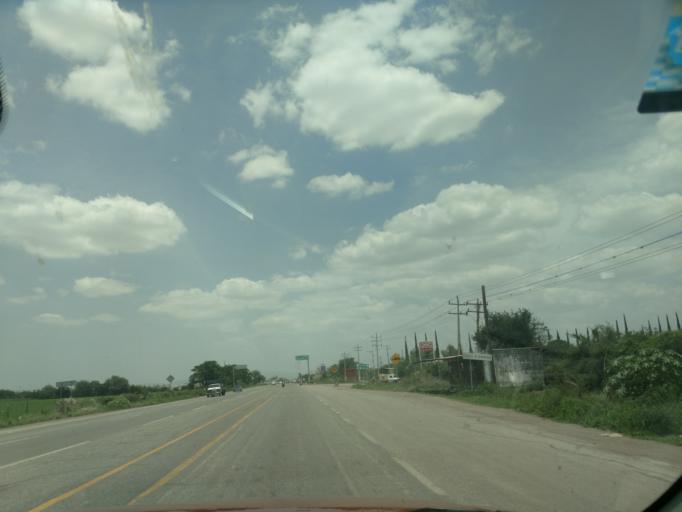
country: MX
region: San Luis Potosi
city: Ciudad Fernandez
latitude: 21.9423
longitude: -100.0432
